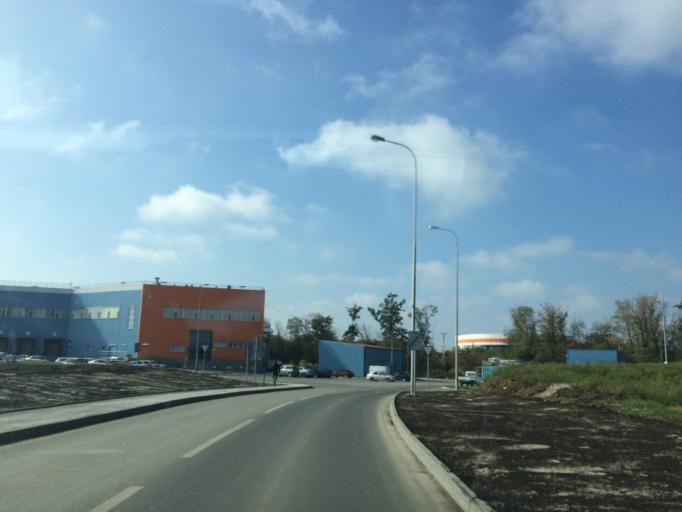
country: RU
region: Rostov
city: Aksay
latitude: 47.2863
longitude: 39.8455
